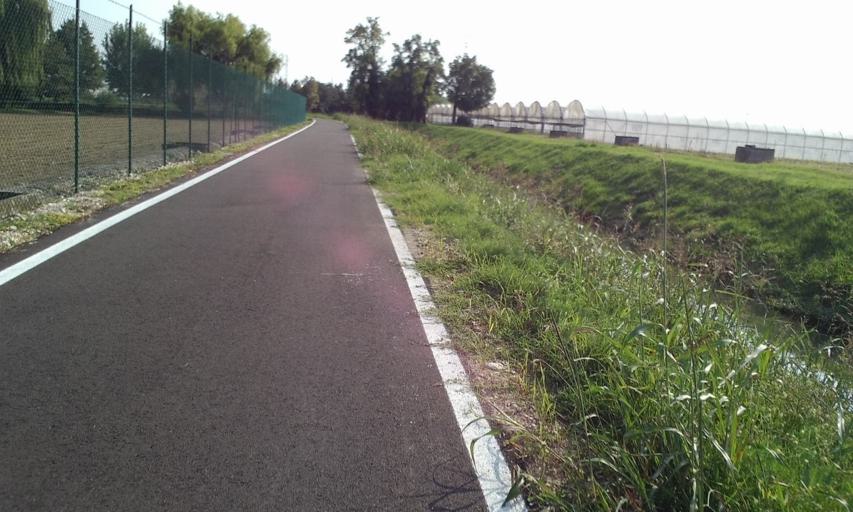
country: IT
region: Veneto
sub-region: Provincia di Verona
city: Buttapietra
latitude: 45.3521
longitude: 10.9864
